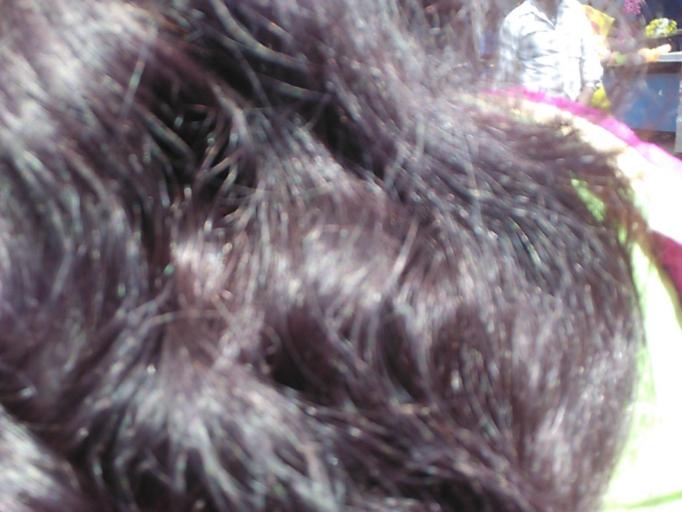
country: IN
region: Tamil Nadu
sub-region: Tiruchchirappalli
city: Tiruchirappalli
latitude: 10.8292
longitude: 78.6947
